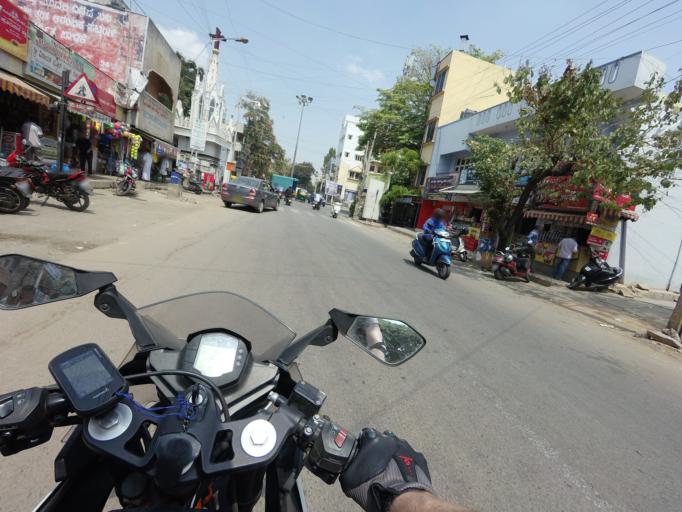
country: IN
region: Karnataka
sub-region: Bangalore Urban
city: Bangalore
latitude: 13.0141
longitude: 77.6397
